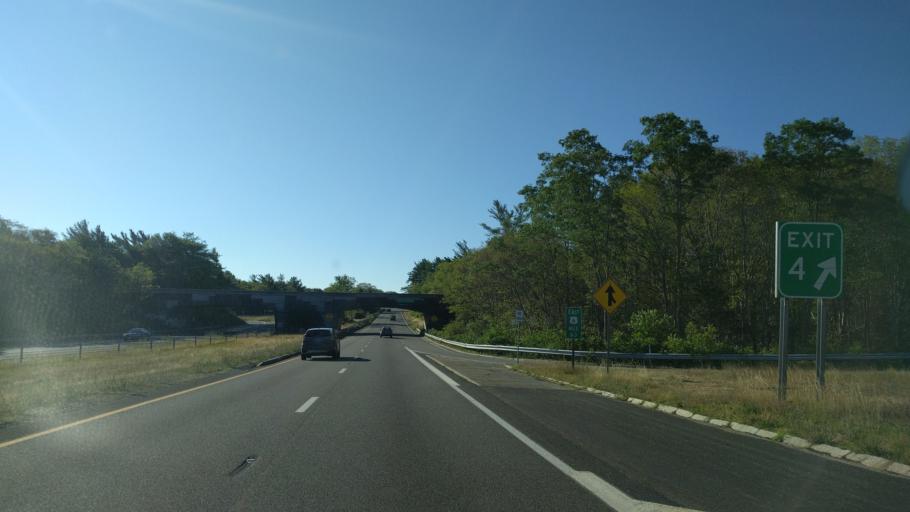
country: US
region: Massachusetts
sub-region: Barnstable County
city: East Sandwich
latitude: 41.7176
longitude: -70.4221
